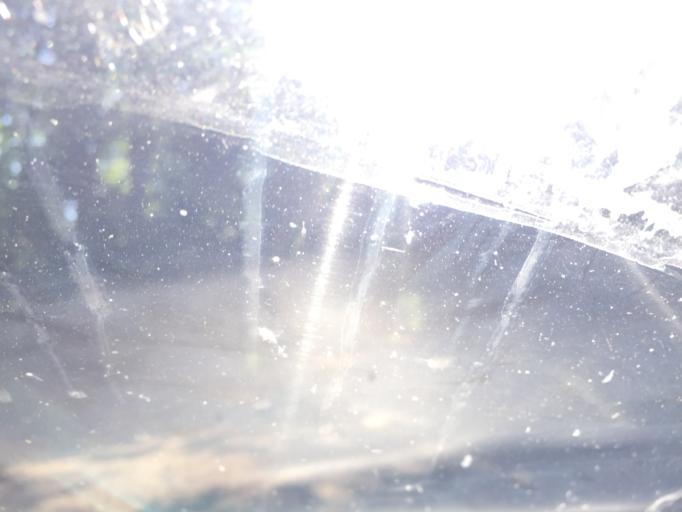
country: DK
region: Capital Region
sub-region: Hoje-Taastrup Kommune
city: Taastrup
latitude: 55.6850
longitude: 12.3164
